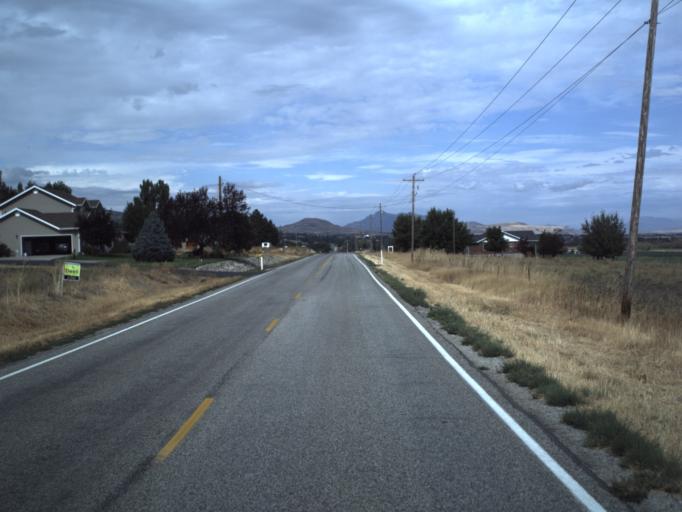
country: US
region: Utah
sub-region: Cache County
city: Wellsville
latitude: 41.6690
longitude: -111.9524
